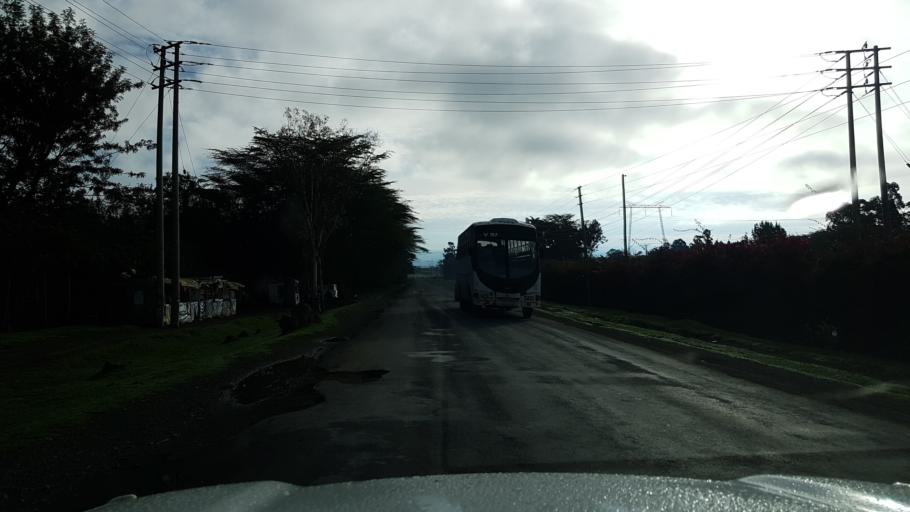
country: KE
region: Nakuru
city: Naivasha
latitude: -0.8265
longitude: 36.3765
